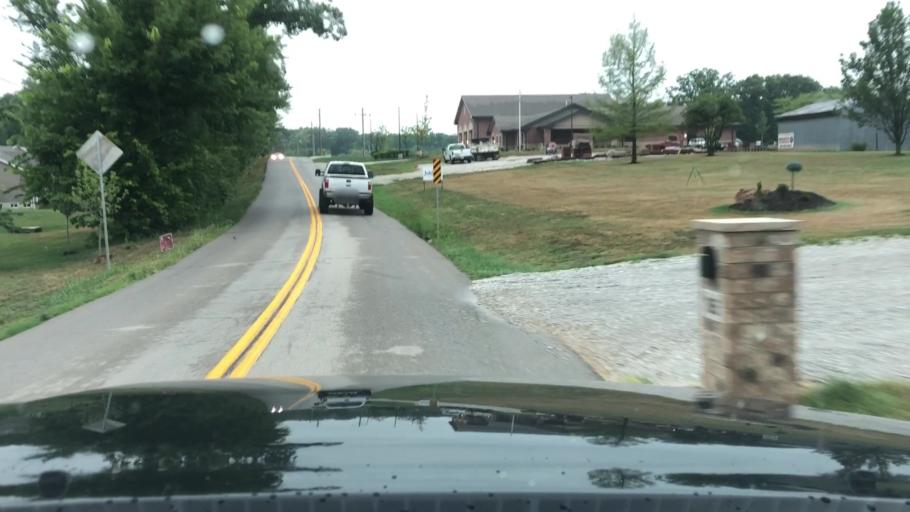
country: US
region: Missouri
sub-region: Saint Charles County
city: Wentzville
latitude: 38.8505
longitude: -90.8780
